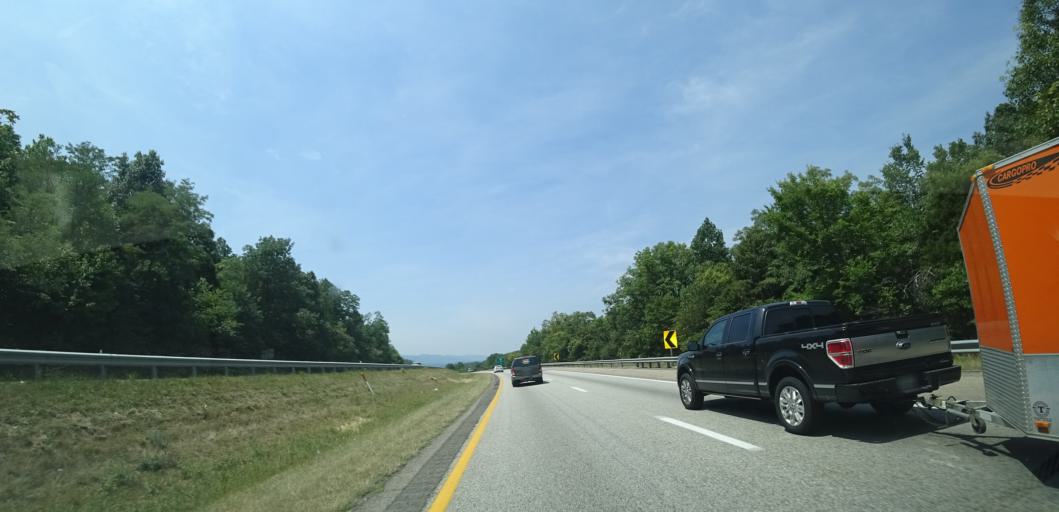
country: US
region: Virginia
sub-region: Botetourt County
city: Buchanan
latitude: 37.5621
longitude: -79.6560
